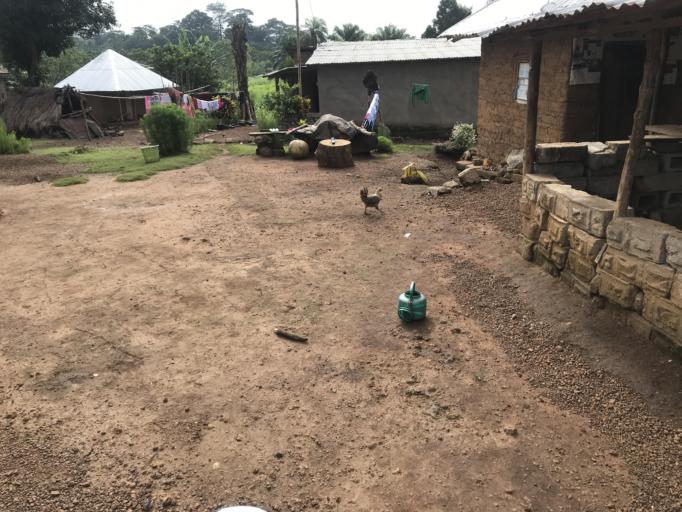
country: SL
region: Eastern Province
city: Buedu
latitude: 8.4672
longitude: -10.3353
